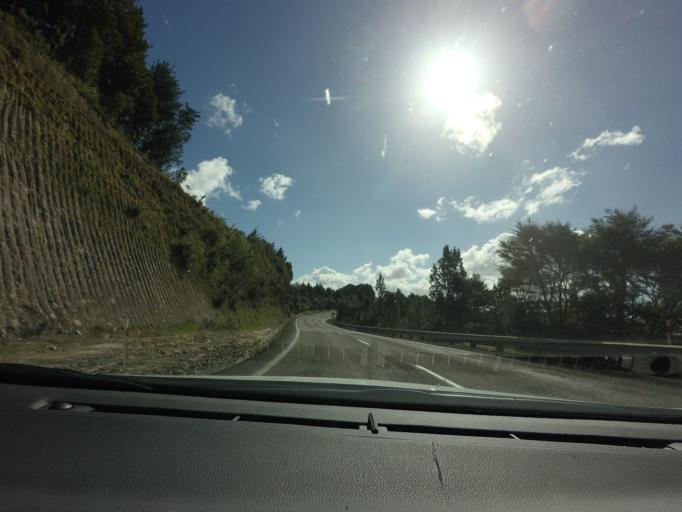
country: NZ
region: Waikato
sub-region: South Waikato District
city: Tokoroa
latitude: -38.0052
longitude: 175.9206
